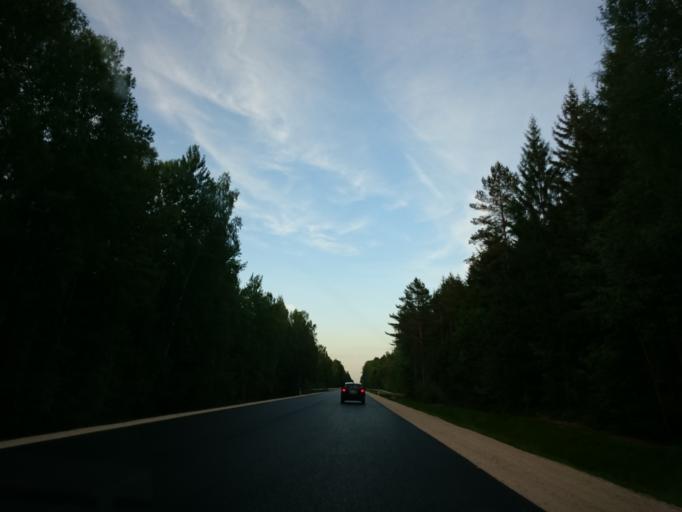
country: LV
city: Tireli
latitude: 56.8206
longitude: 23.5142
